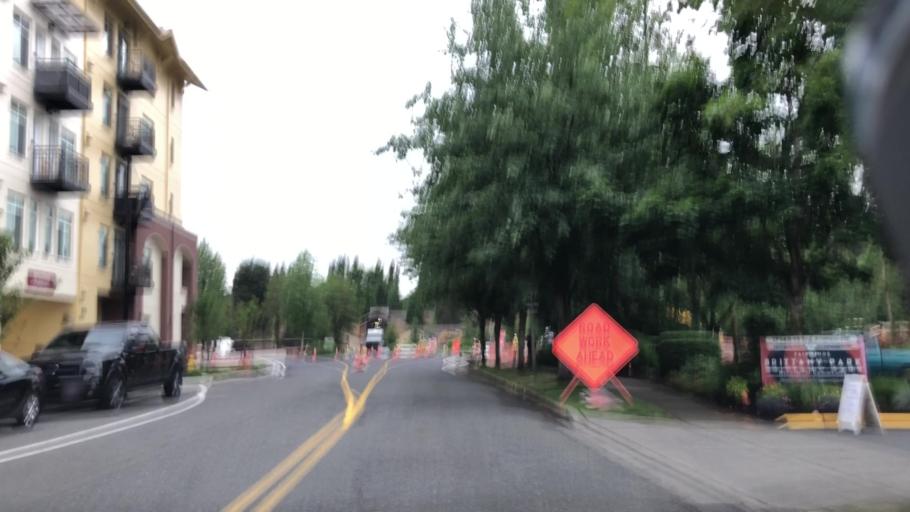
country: US
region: Washington
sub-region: King County
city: Woodinville
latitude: 47.7516
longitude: -122.1614
